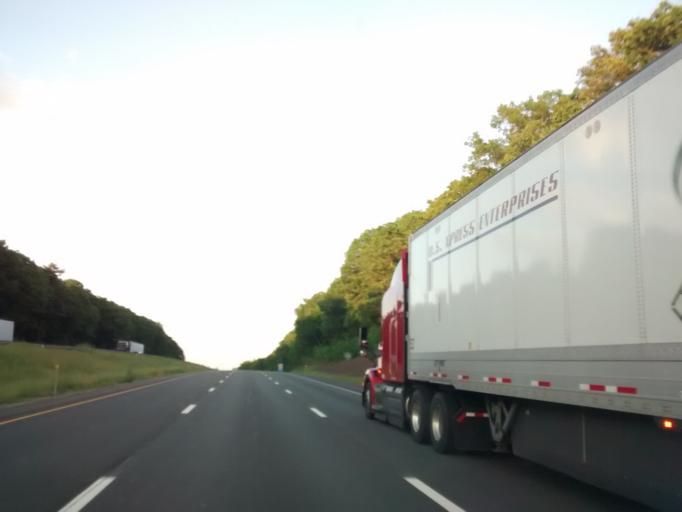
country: US
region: Connecticut
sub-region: Tolland County
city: Tolland
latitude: 41.8553
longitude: -72.3803
